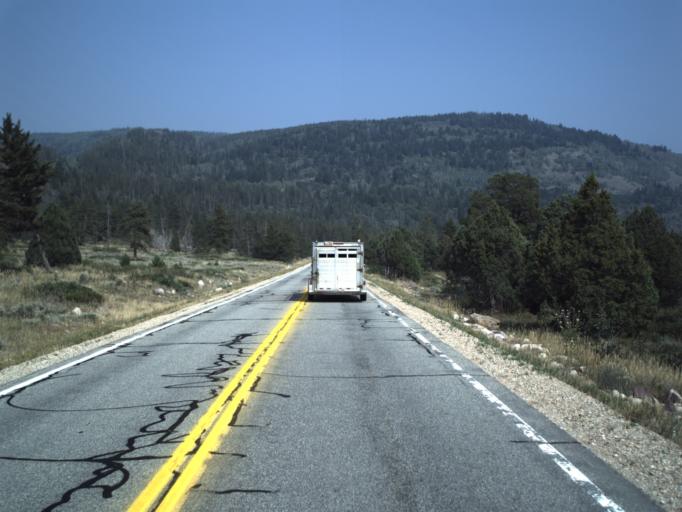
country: US
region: Utah
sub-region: Summit County
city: Francis
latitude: 40.5945
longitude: -111.0858
